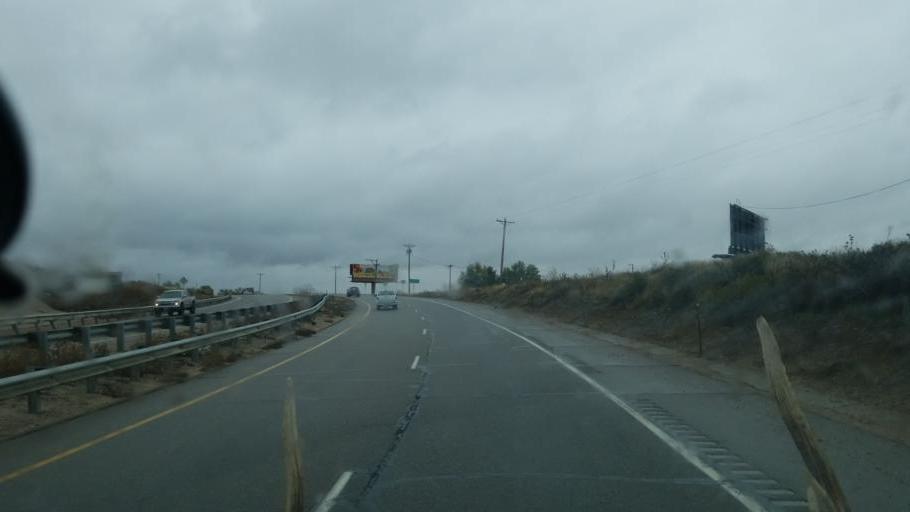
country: US
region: Colorado
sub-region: Pueblo County
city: Pueblo
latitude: 38.2715
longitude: -104.5517
